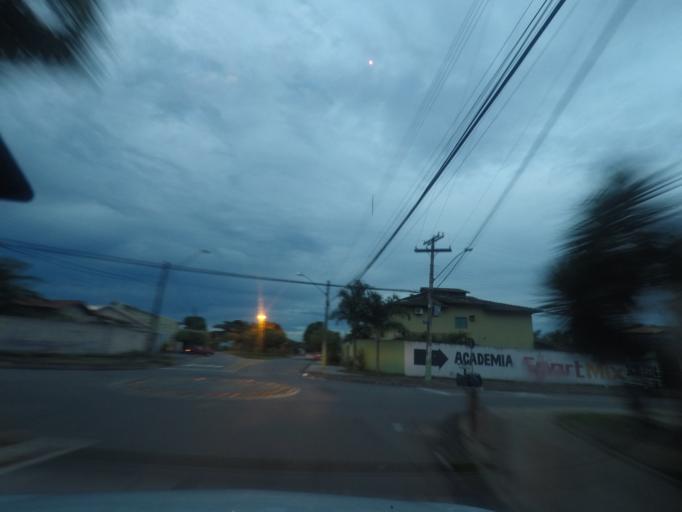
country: BR
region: Goias
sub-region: Goiania
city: Goiania
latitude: -16.7176
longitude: -49.3021
